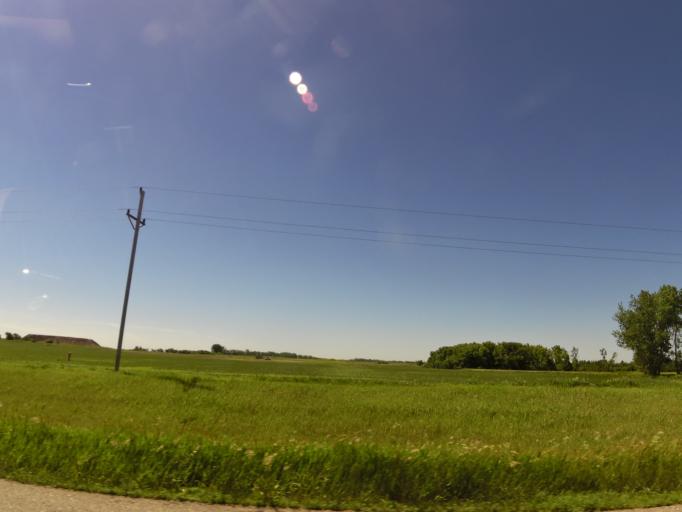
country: US
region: Minnesota
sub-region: Red Lake County
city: Red Lake Falls
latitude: 47.7603
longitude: -96.3460
